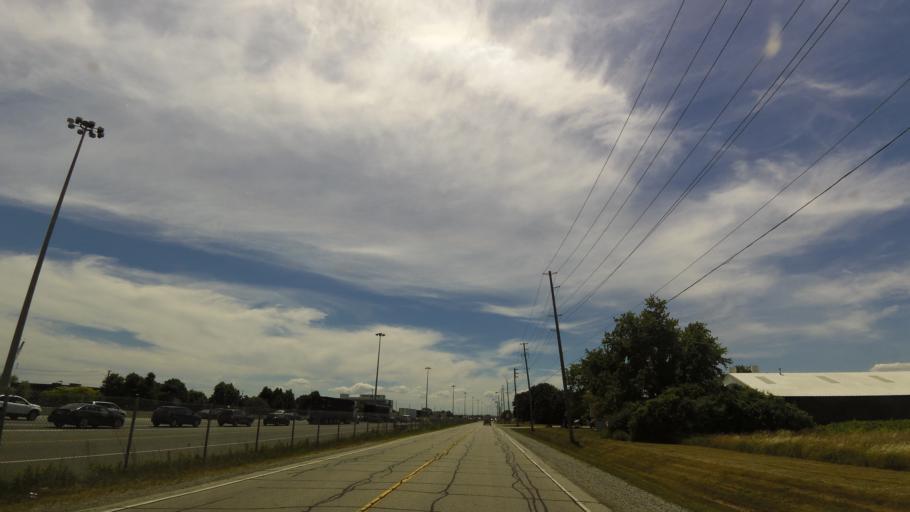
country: CA
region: Ontario
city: Burlington
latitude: 43.3785
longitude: -79.7754
